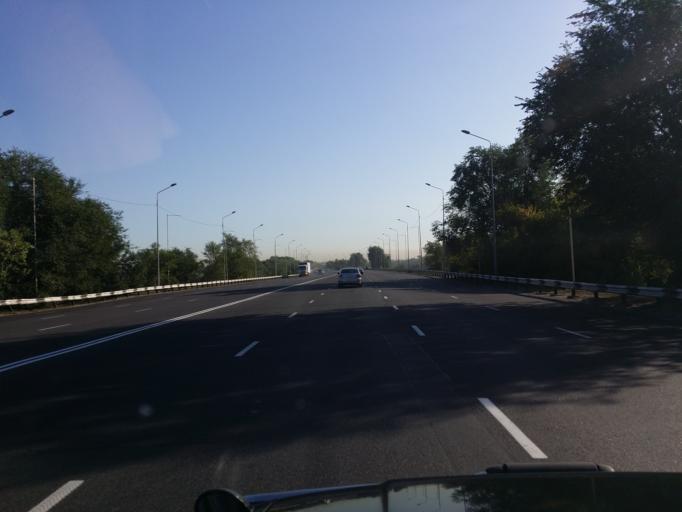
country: KZ
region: Almaty Oblysy
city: Pervomayskiy
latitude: 43.3473
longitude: 76.9341
